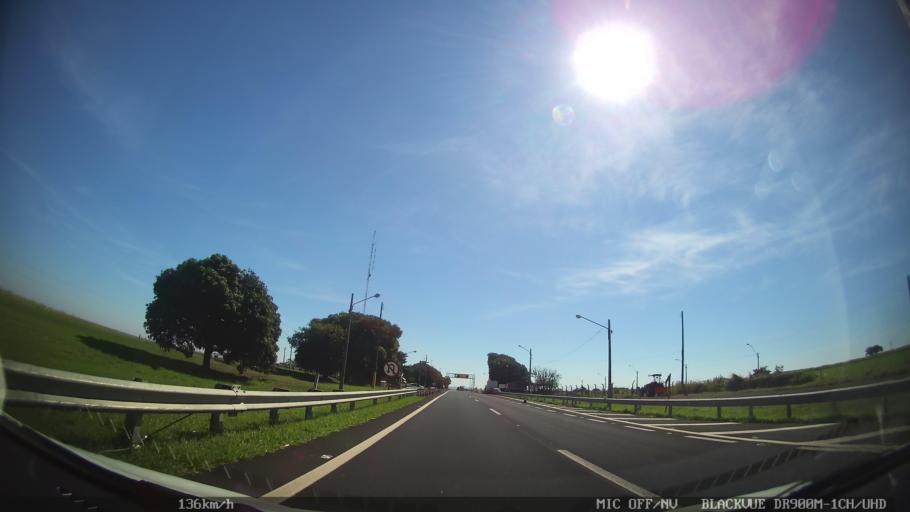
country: BR
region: Sao Paulo
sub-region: Santa Rita Do Passa Quatro
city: Santa Rita do Passa Quatro
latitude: -21.6855
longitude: -47.6013
